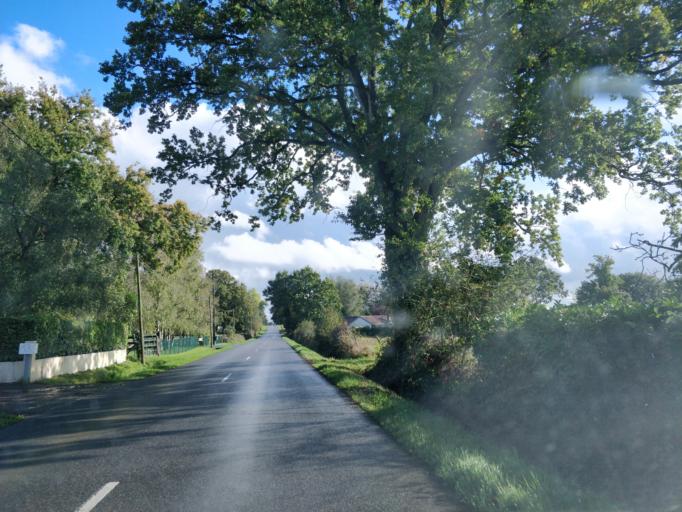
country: FR
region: Brittany
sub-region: Departement d'Ille-et-Vilaine
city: La Bouexiere
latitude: 48.1677
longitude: -1.4258
